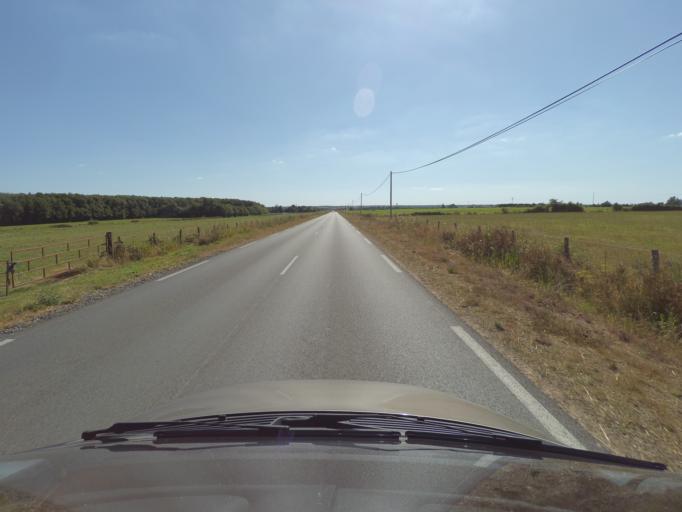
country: FR
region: Pays de la Loire
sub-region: Departement de Maine-et-Loire
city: Torfou
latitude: 47.0304
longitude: -1.0956
